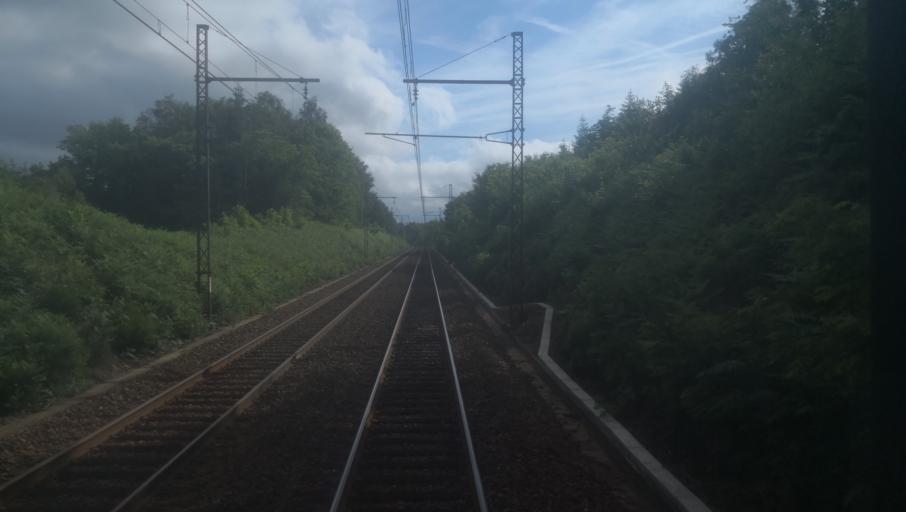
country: FR
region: Limousin
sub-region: Departement de la Haute-Vienne
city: Saint-Priest-Taurion
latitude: 45.8979
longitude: 1.3690
